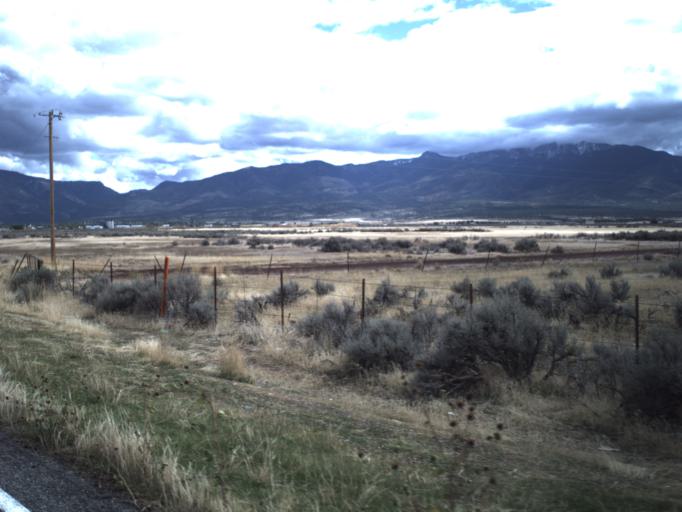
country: US
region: Utah
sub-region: Millard County
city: Fillmore
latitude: 38.9791
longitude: -112.3730
